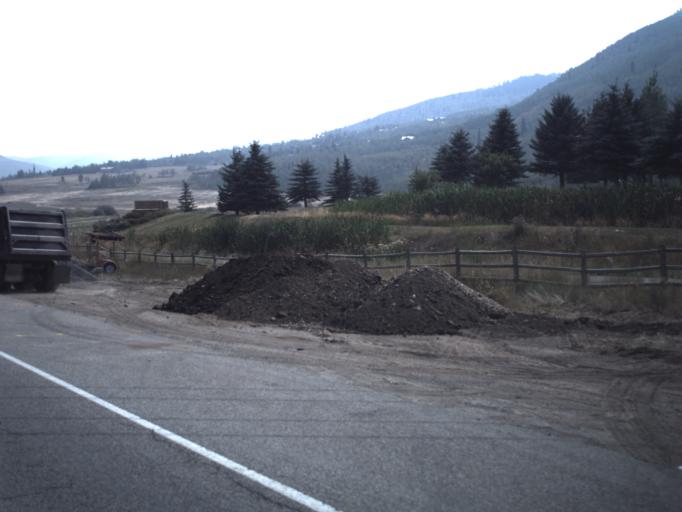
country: US
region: Utah
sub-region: Summit County
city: Snyderville
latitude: 40.6832
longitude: -111.5368
